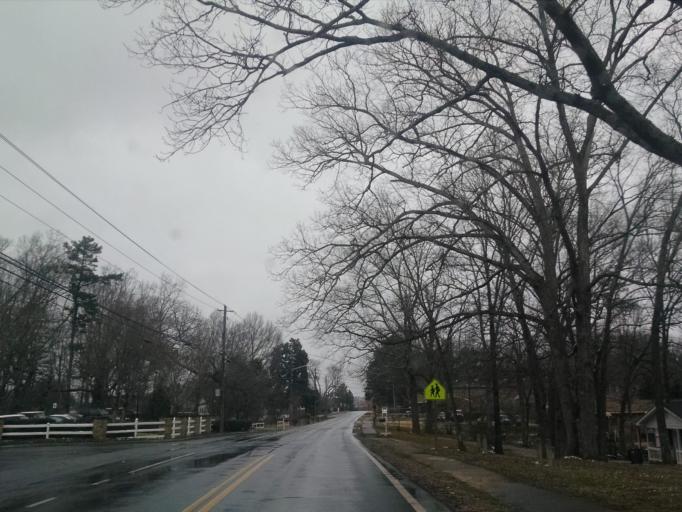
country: US
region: Georgia
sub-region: Gwinnett County
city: Sugar Hill
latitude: 34.1025
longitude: -84.0391
